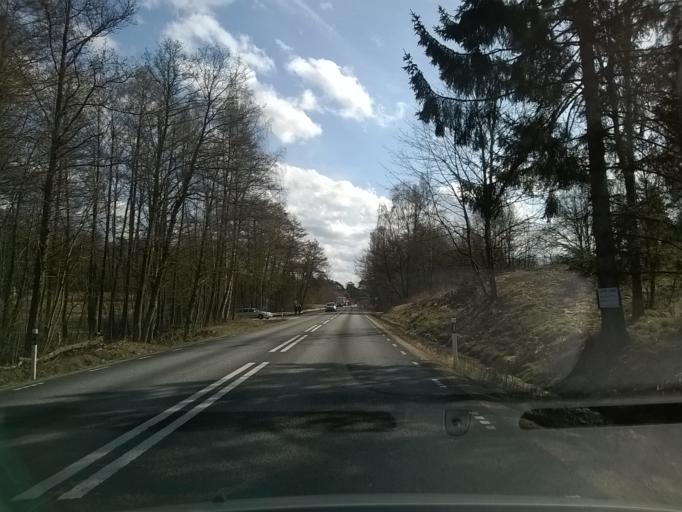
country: SE
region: Vaestra Goetaland
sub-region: Orust
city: Henan
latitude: 58.3179
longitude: 11.6829
